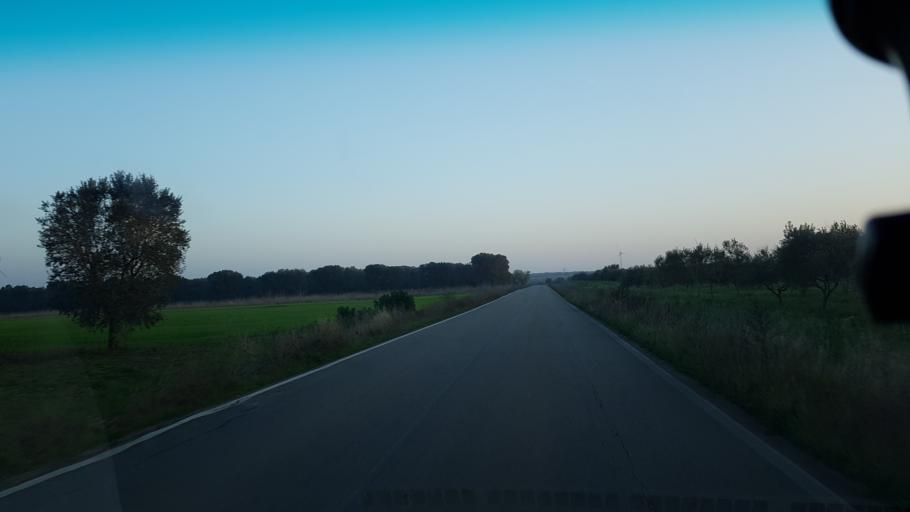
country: IT
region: Apulia
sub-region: Provincia di Brindisi
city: Mesagne
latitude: 40.6254
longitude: 17.7841
